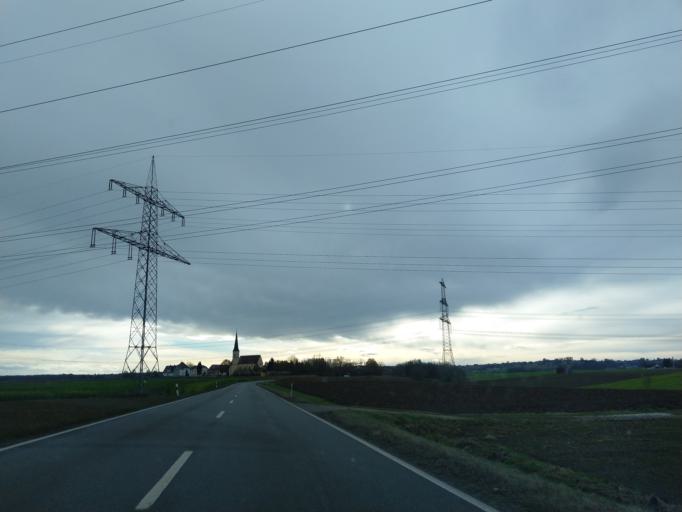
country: DE
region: Bavaria
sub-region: Lower Bavaria
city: Kunzing
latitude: 48.6575
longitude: 13.0465
